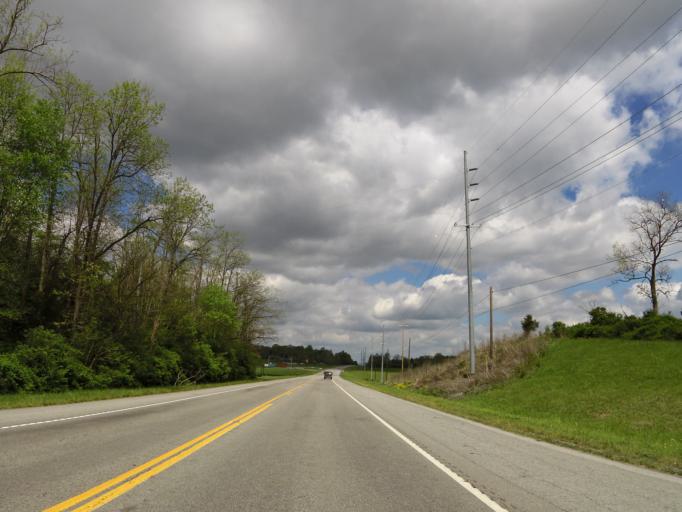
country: US
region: Kentucky
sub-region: Bell County
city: Middlesboro
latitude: 36.4826
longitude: -83.8393
